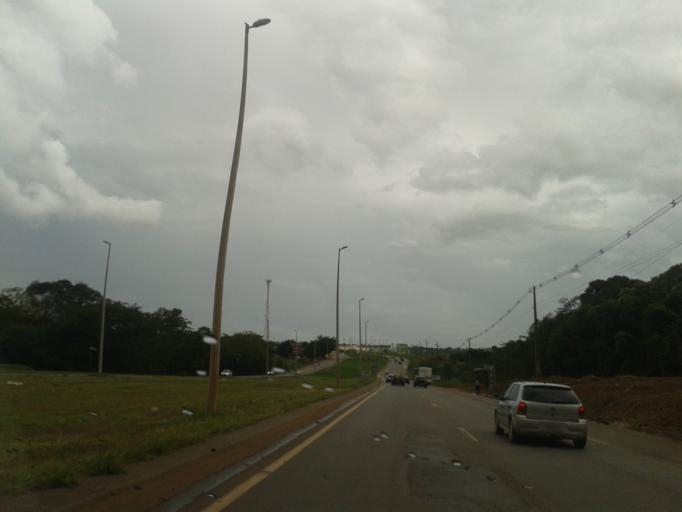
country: BR
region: Goias
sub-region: Goianira
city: Goianira
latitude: -16.5859
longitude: -49.3839
